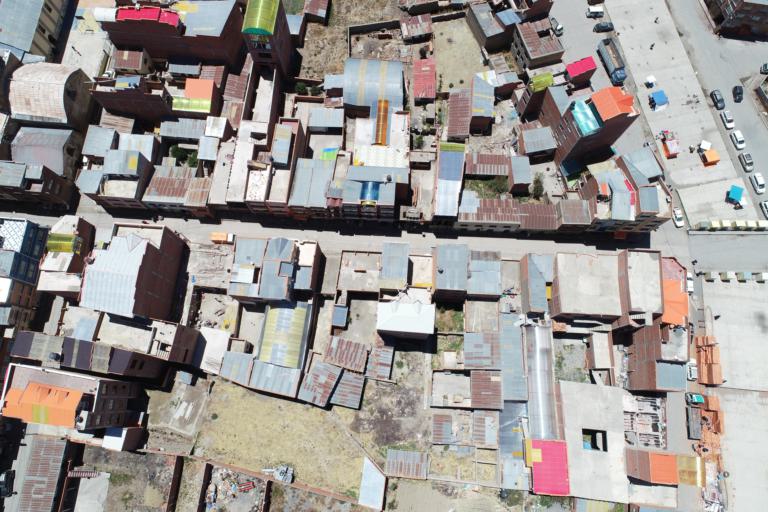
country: BO
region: La Paz
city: Achacachi
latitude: -16.0438
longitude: -68.6865
